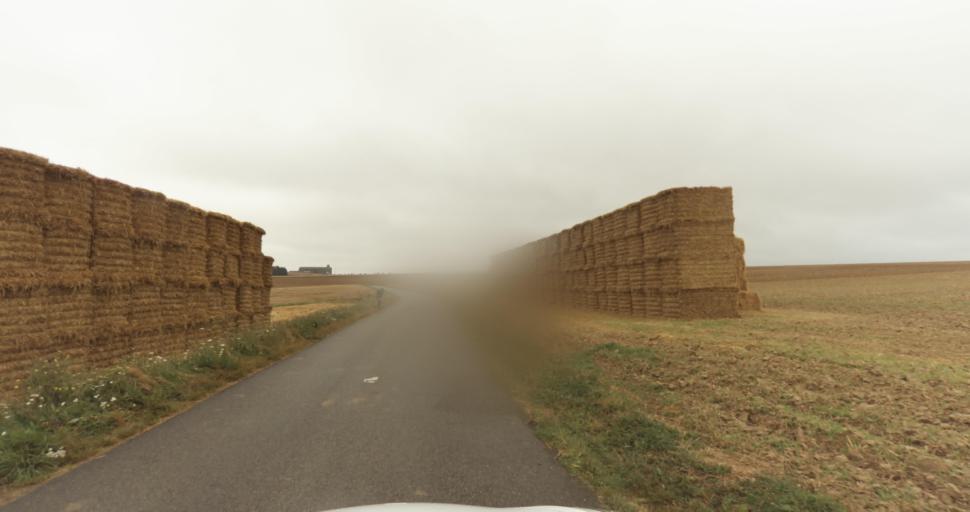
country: FR
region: Haute-Normandie
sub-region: Departement de l'Eure
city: Gravigny
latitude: 49.0794
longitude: 1.2134
